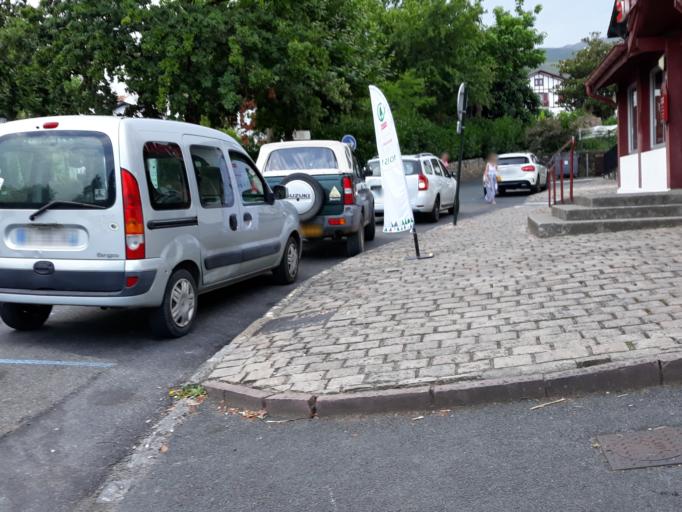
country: FR
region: Aquitaine
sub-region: Departement des Pyrenees-Atlantiques
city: Ascain
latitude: 43.3464
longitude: -1.6220
